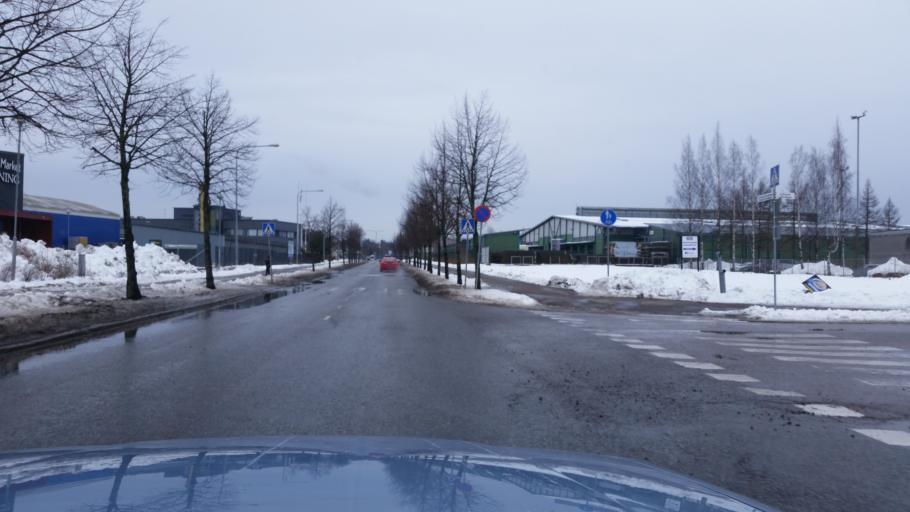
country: FI
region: Uusimaa
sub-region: Helsinki
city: Vantaa
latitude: 60.2797
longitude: 25.0116
